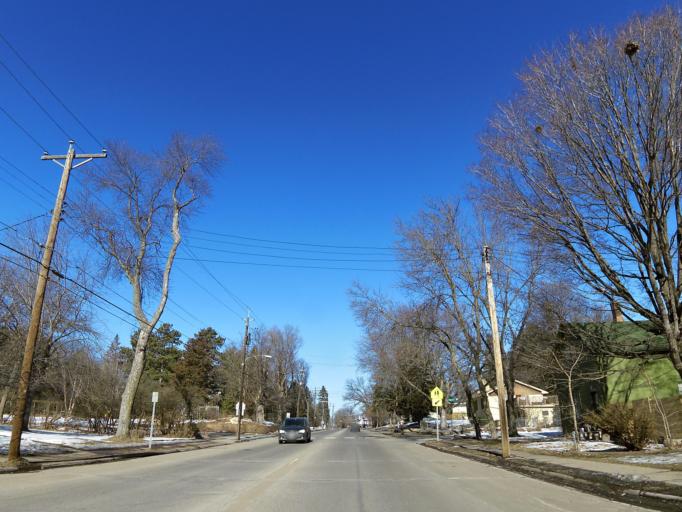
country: US
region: Minnesota
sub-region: Washington County
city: Stillwater
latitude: 45.0625
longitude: -92.8205
